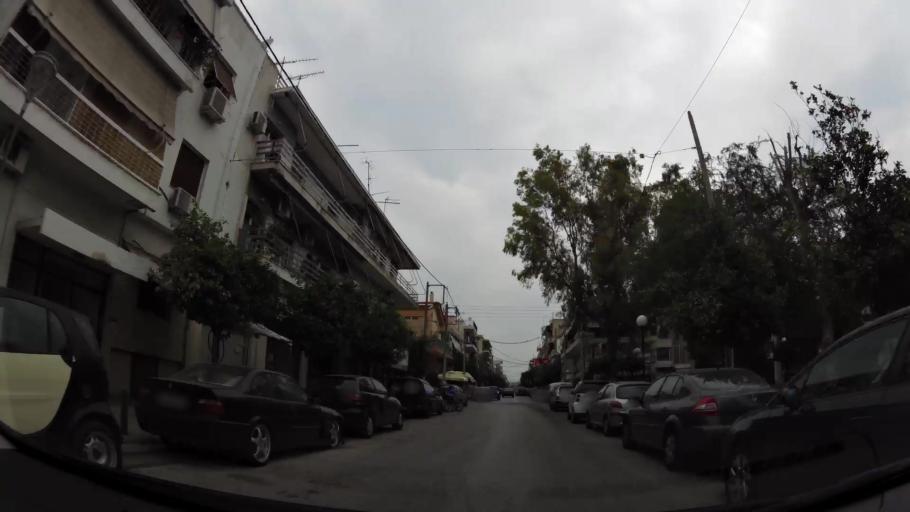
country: GR
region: Attica
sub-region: Nomarchia Athinas
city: Aigaleo
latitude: 37.9953
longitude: 23.6828
